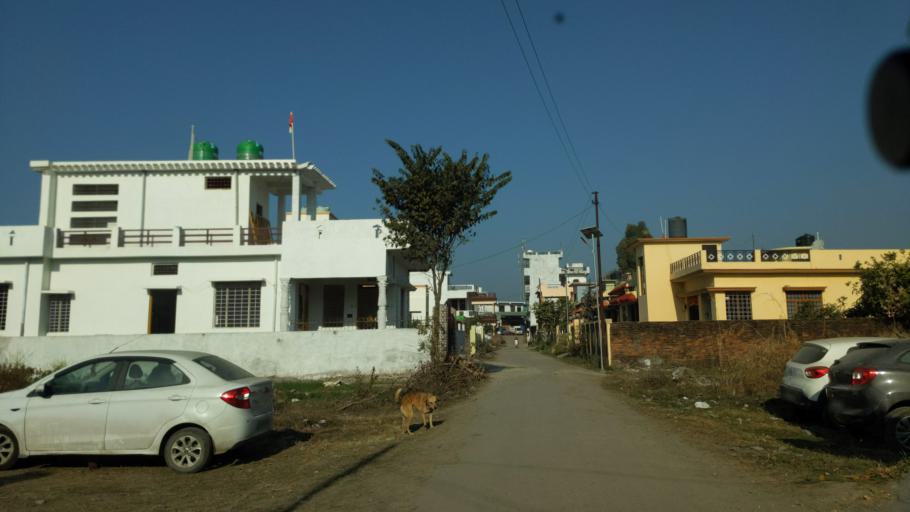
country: IN
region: Uttarakhand
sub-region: Naini Tal
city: Haldwani
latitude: 29.2072
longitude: 79.4960
